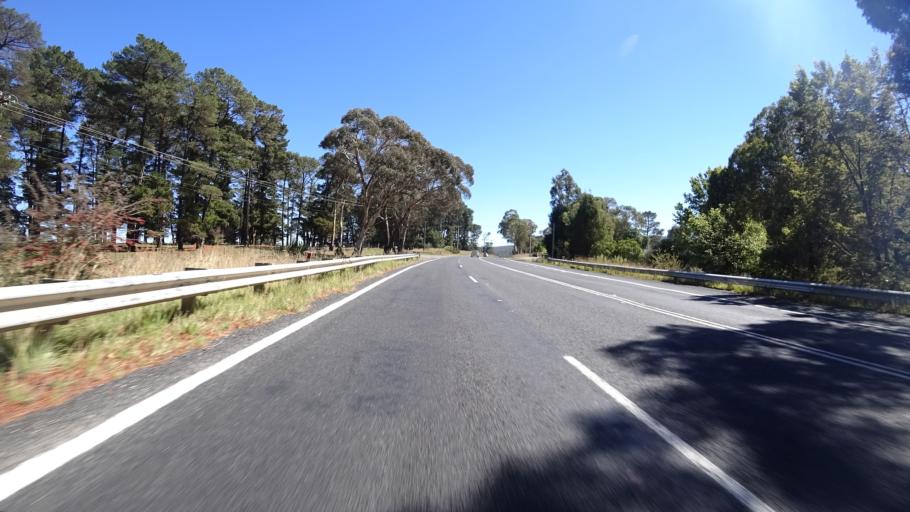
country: AU
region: New South Wales
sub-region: Lithgow
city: Portland
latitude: -33.3752
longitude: 150.0730
